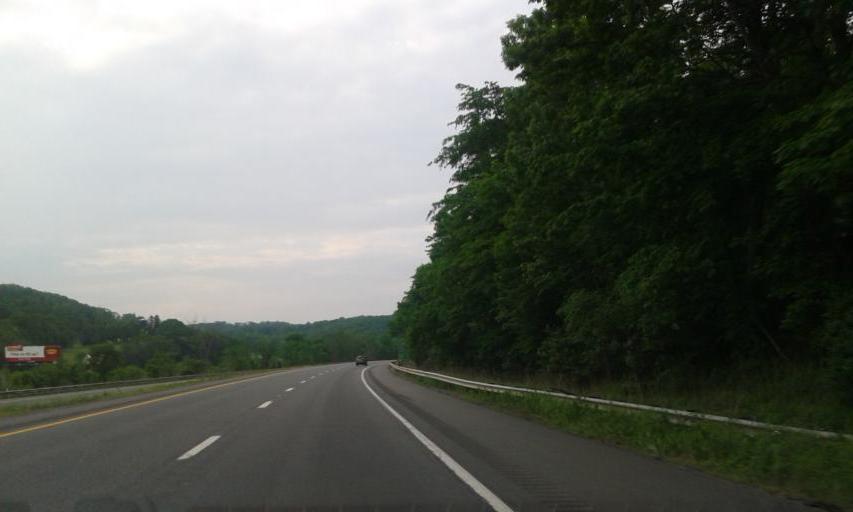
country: US
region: Pennsylvania
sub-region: Susquehanna County
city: Susquehanna
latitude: 41.7607
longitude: -75.6858
